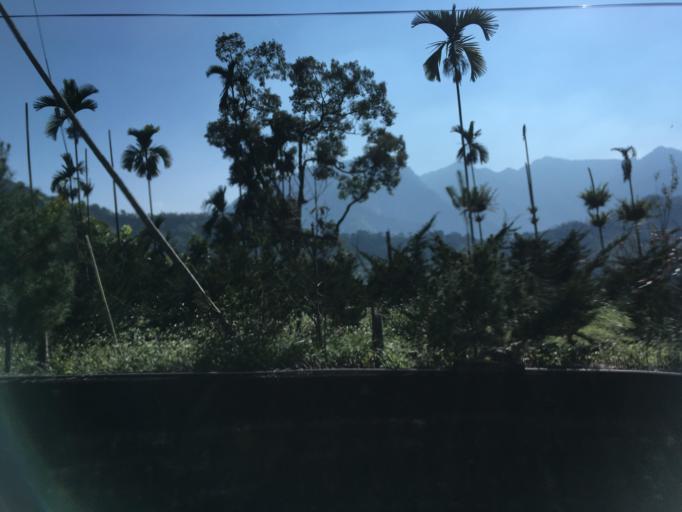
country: TW
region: Taiwan
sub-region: Chiayi
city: Jiayi Shi
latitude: 23.4344
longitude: 120.6301
